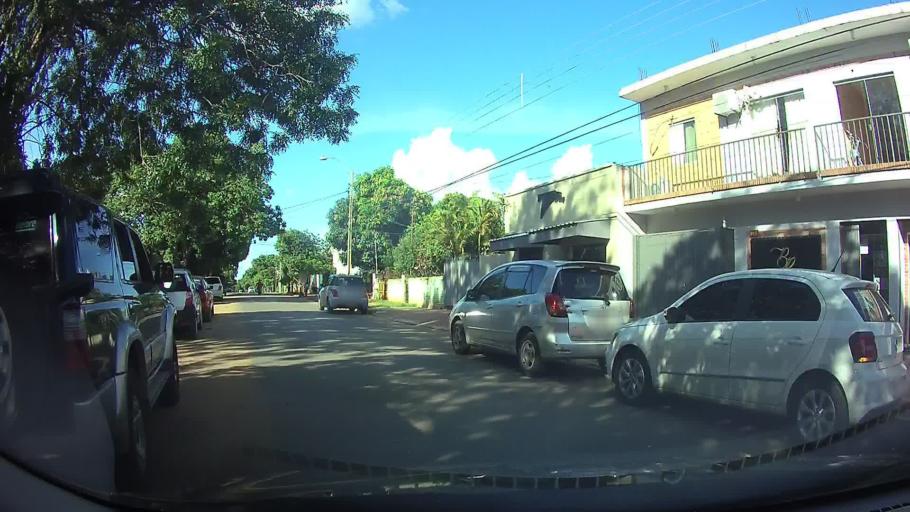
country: PY
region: Central
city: San Lorenzo
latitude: -25.2714
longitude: -57.4845
